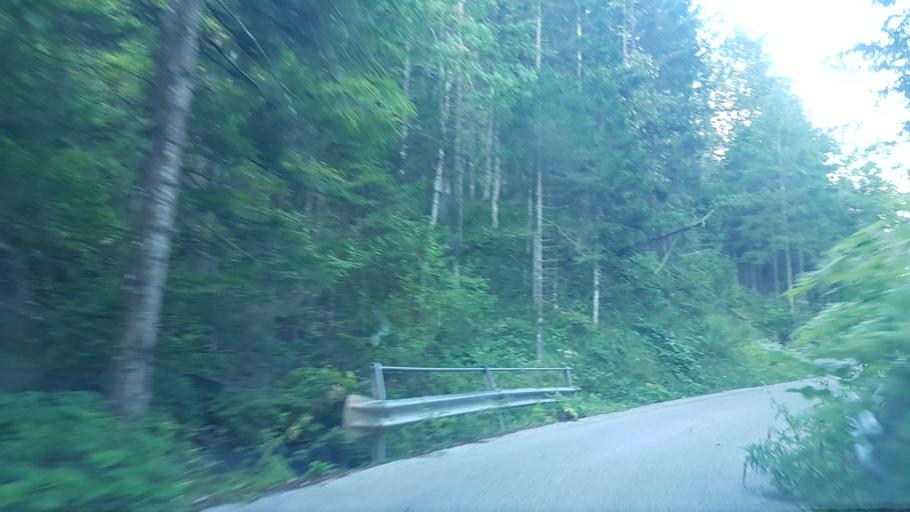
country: IT
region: Friuli Venezia Giulia
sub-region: Provincia di Udine
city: Tarvisio
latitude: 46.4910
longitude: 13.5895
